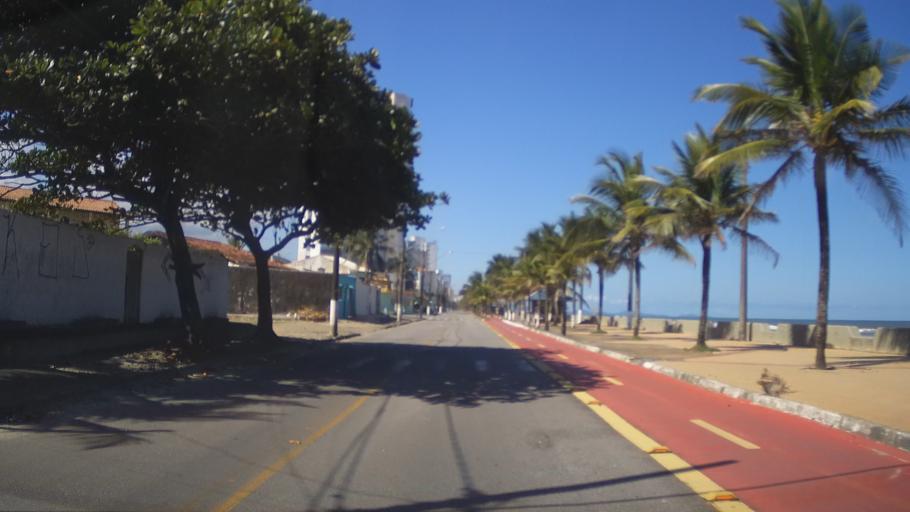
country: BR
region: Sao Paulo
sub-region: Mongagua
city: Mongagua
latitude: -24.1120
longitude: -46.6513
